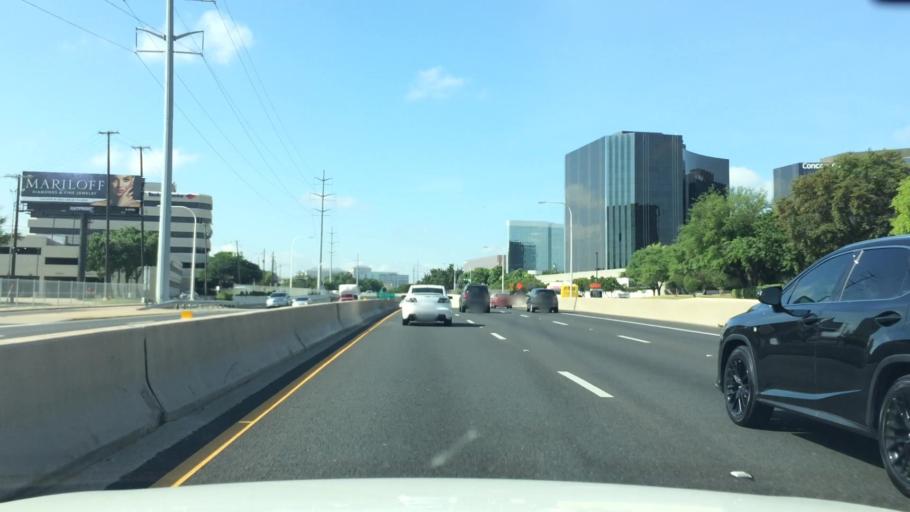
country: US
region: Texas
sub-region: Dallas County
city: Addison
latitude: 32.9570
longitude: -96.8216
